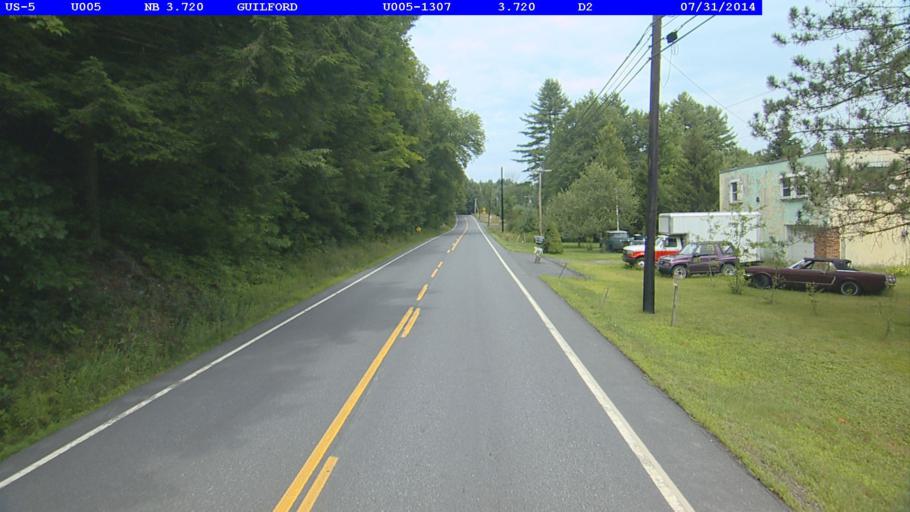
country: US
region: Vermont
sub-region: Windham County
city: Brattleboro
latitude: 42.7820
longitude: -72.5700
